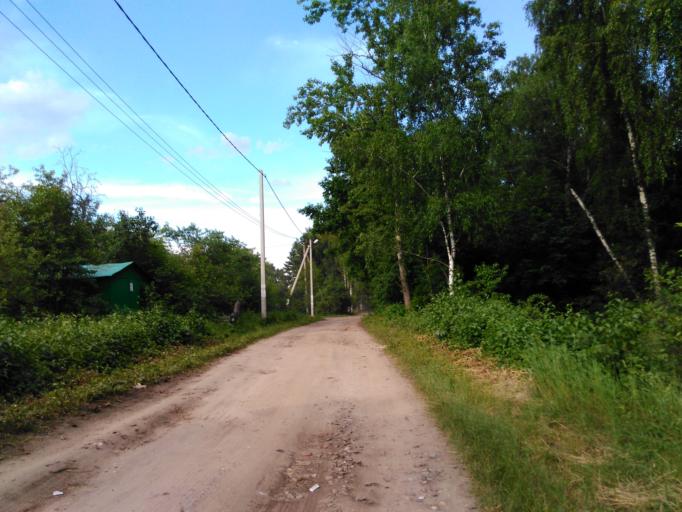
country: RU
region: Moskovskaya
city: Vishnyakovskiye Dachi
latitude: 55.7634
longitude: 38.1426
